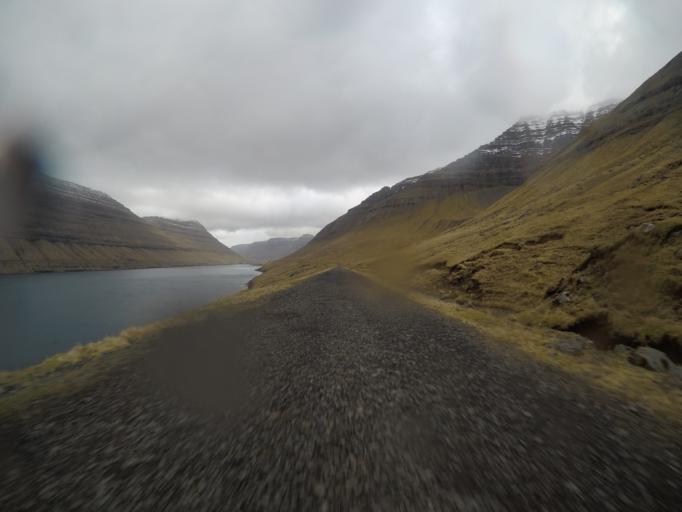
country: FO
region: Nordoyar
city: Klaksvik
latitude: 62.3228
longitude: -6.5610
